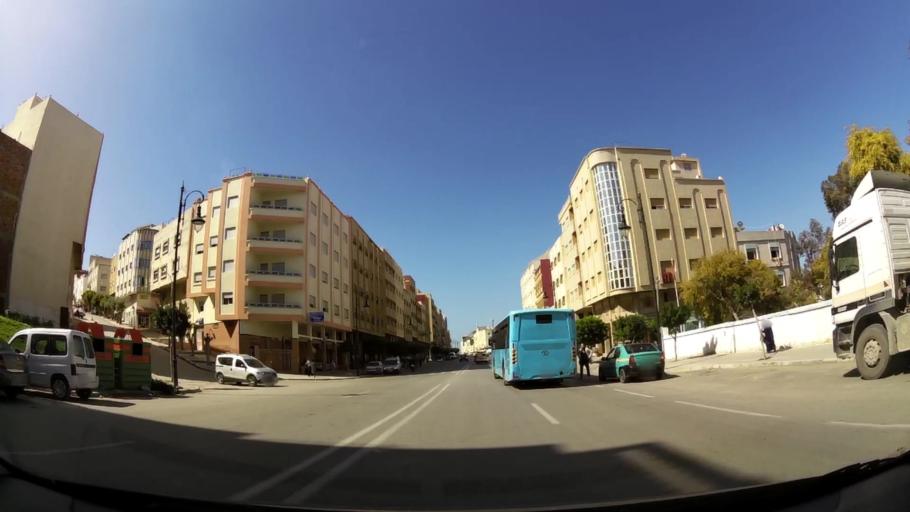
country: MA
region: Tanger-Tetouan
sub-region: Tanger-Assilah
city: Tangier
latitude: 35.7443
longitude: -5.8071
